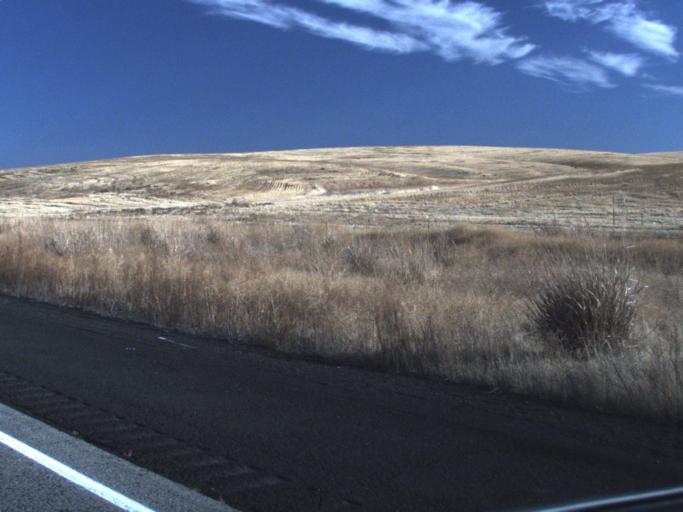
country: US
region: Washington
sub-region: Adams County
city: Ritzville
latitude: 47.0827
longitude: -118.4110
